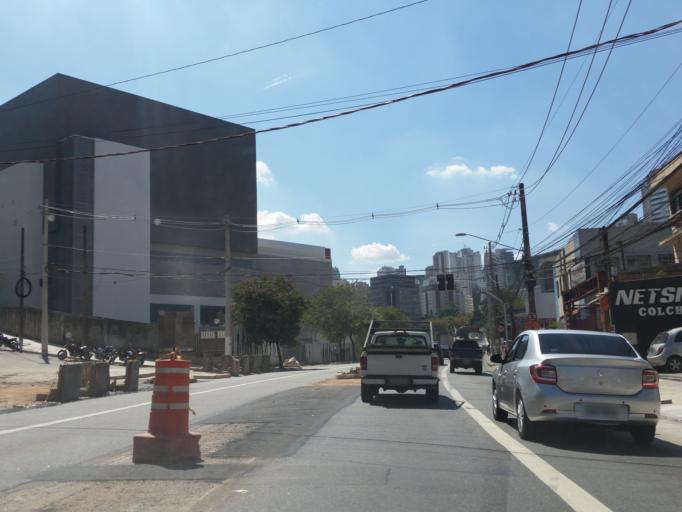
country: BR
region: Sao Paulo
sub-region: Taboao Da Serra
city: Taboao da Serra
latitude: -23.6332
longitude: -46.7370
